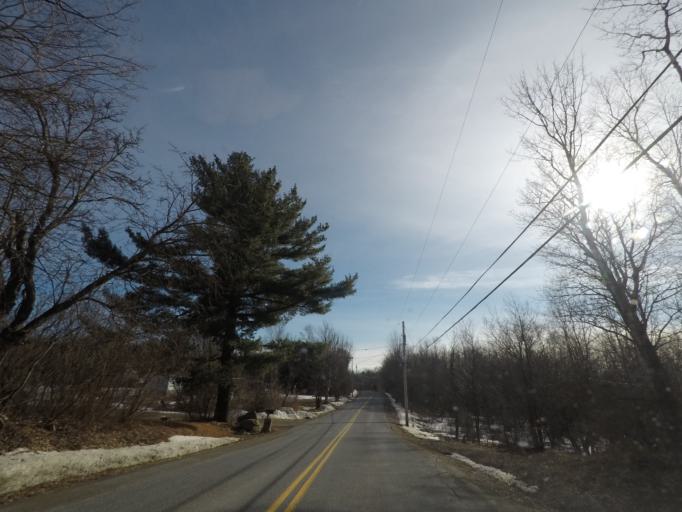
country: US
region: New York
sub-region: Rensselaer County
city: Poestenkill
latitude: 42.7115
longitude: -73.4205
